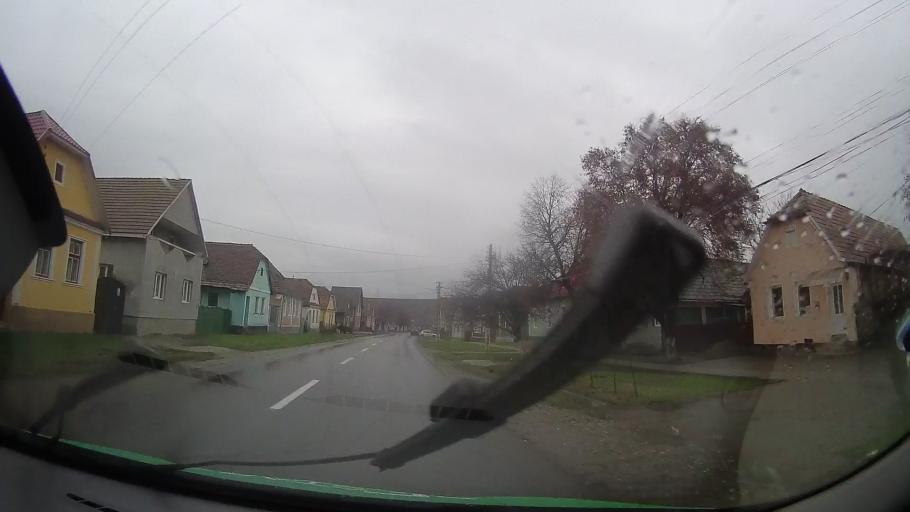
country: RO
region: Bistrita-Nasaud
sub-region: Comuna Mariselu
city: Mariselu
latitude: 47.0374
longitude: 24.4751
